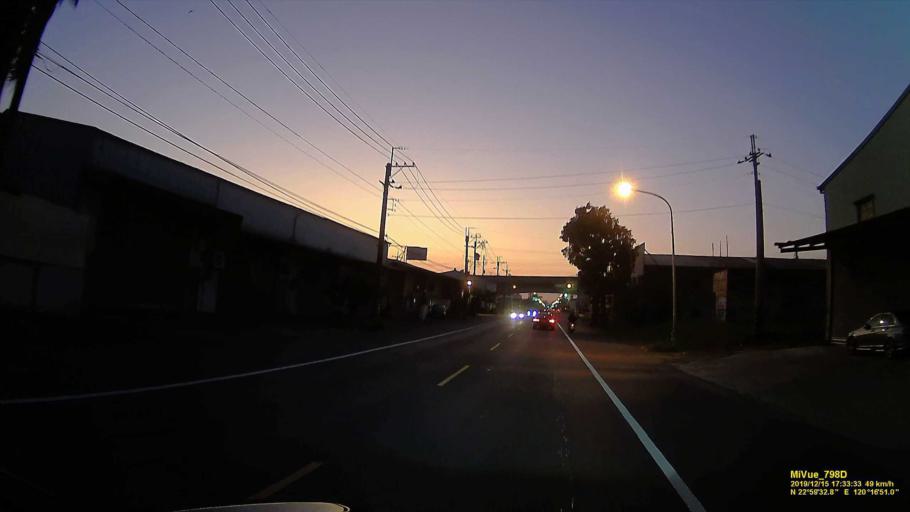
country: TW
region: Taiwan
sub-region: Tainan
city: Tainan
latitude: 22.9924
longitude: 120.2806
